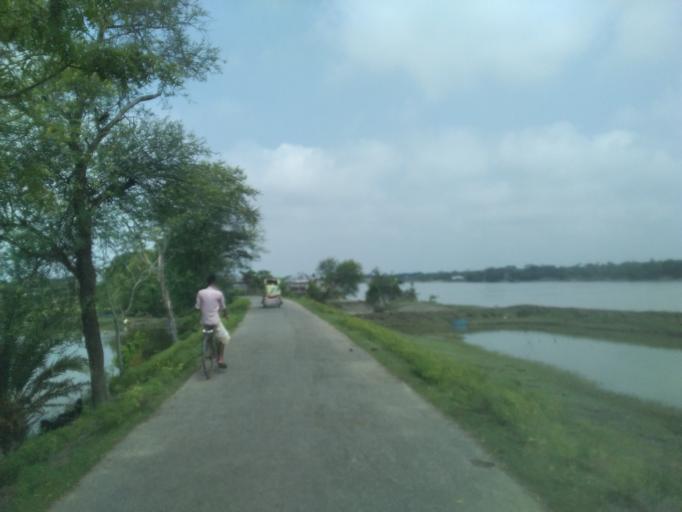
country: BD
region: Khulna
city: Phultala
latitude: 22.7046
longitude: 89.4662
